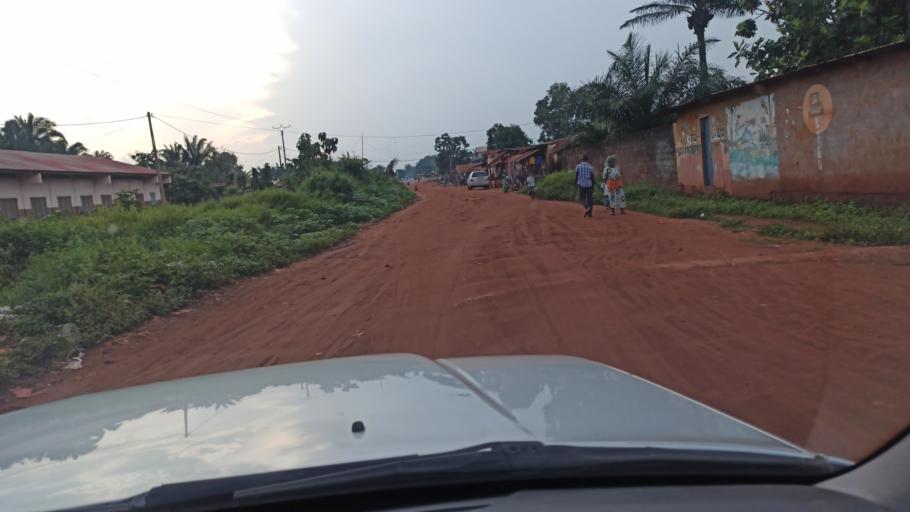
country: BJ
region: Queme
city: Porto-Novo
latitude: 6.5348
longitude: 2.6501
